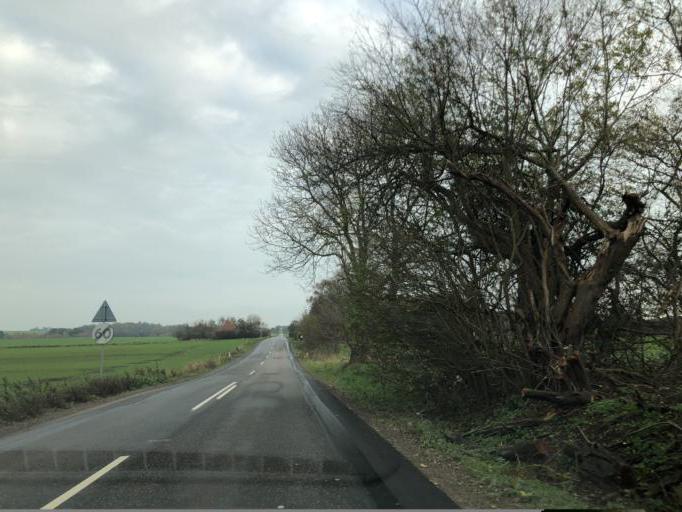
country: DK
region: Central Jutland
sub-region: Hedensted Kommune
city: Hornsyld
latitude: 55.7354
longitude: 9.7751
